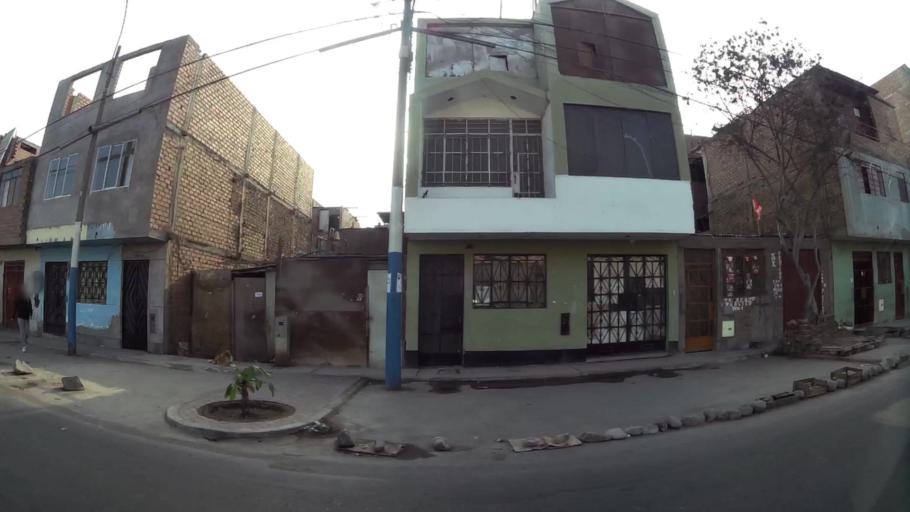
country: PE
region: Lima
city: Lima
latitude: -12.0283
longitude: -77.0725
